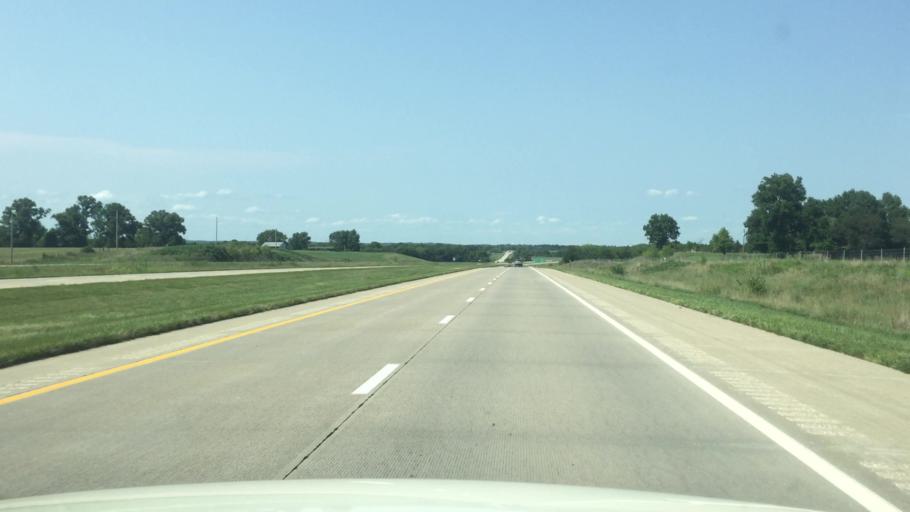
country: US
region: Kansas
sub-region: Linn County
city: Pleasanton
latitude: 38.1269
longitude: -94.7133
